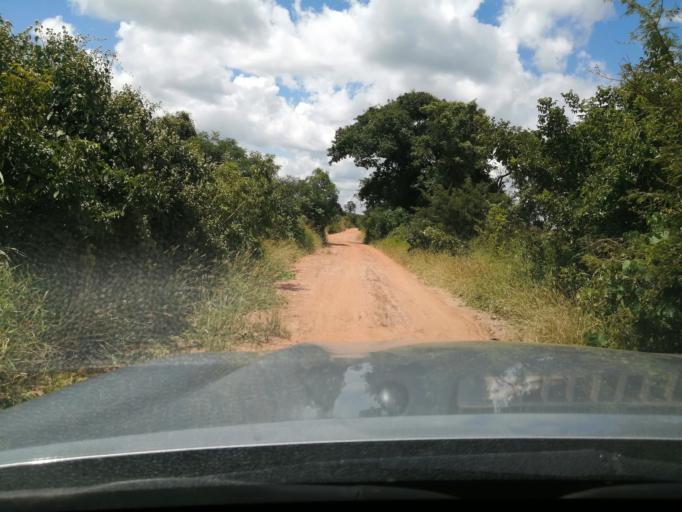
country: ZM
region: Lusaka
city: Lusaka
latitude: -15.1511
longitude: 27.9440
